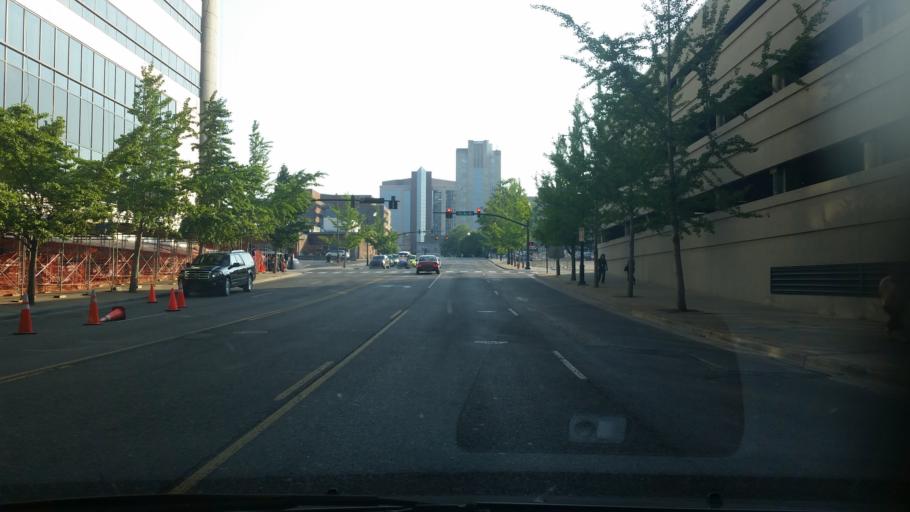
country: US
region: Tennessee
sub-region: Davidson County
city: Nashville
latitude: 36.1611
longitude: -86.7811
